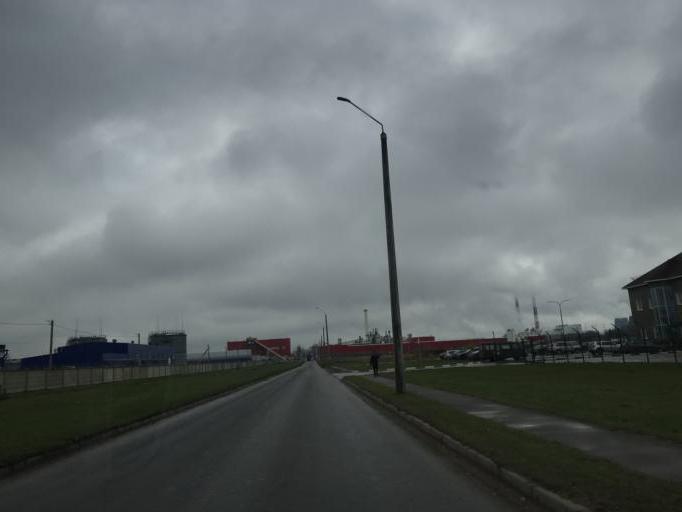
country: BY
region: Mogilev
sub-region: Mahilyowski Rayon
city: Veyno
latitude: 53.8276
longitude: 30.3525
